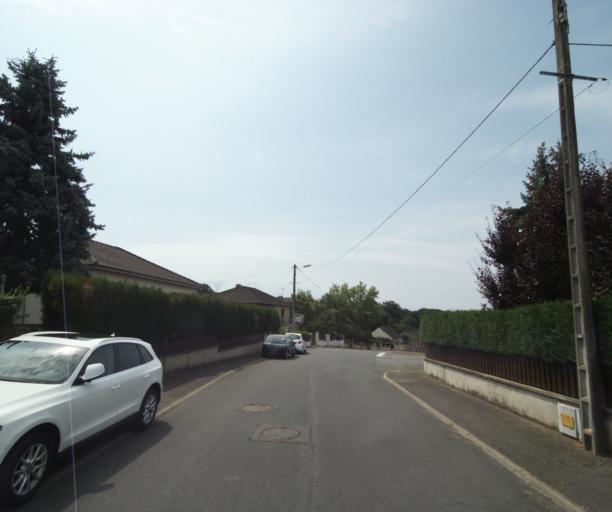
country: FR
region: Bourgogne
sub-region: Departement de Saone-et-Loire
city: Gueugnon
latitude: 46.5942
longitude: 4.0772
